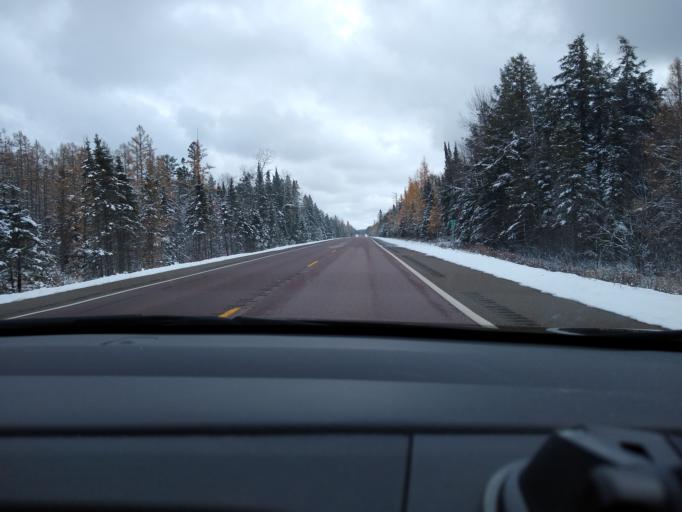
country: US
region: Michigan
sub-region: Iron County
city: Iron River
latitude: 46.1682
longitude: -88.9234
